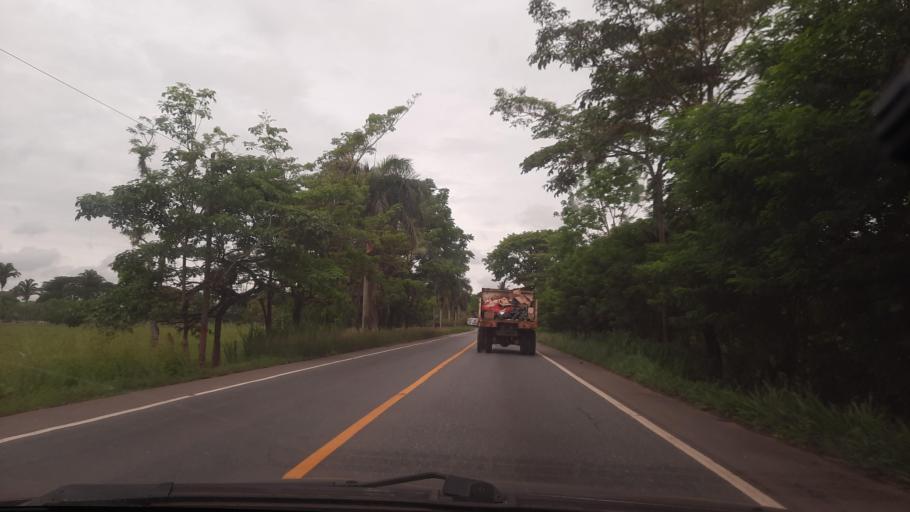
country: GT
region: Izabal
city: Morales
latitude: 15.4694
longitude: -88.9050
